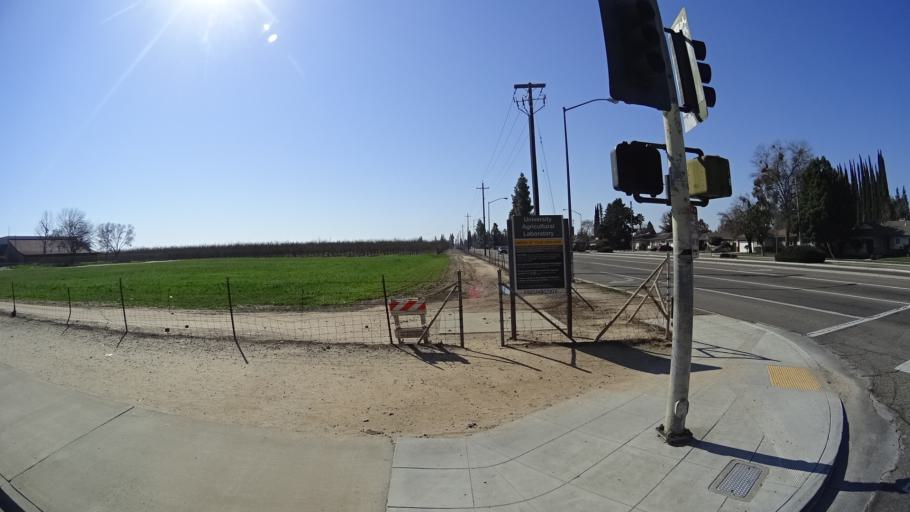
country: US
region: California
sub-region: Fresno County
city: Clovis
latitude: 36.8304
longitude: -119.7540
